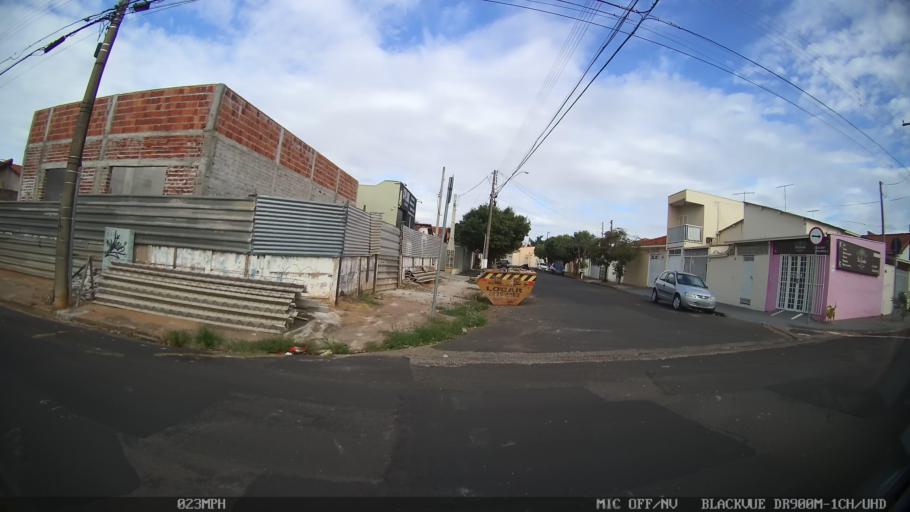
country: BR
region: Sao Paulo
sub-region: Sao Jose Do Rio Preto
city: Sao Jose do Rio Preto
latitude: -20.8346
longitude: -49.3772
